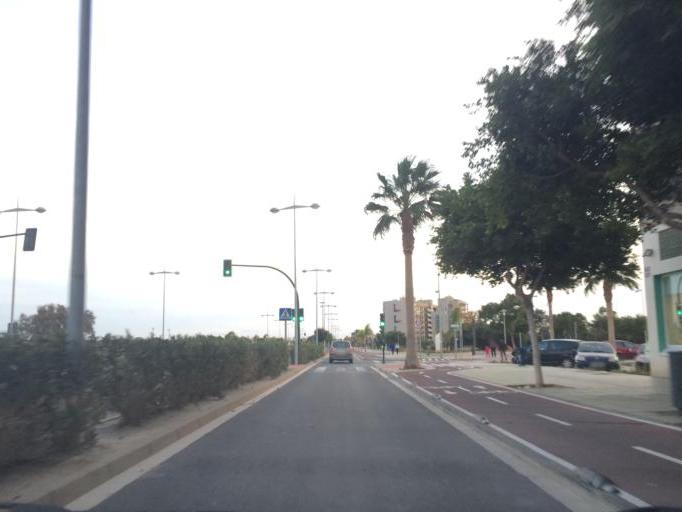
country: ES
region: Andalusia
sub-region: Provincia de Almeria
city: Almeria
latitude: 36.8308
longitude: -2.4381
